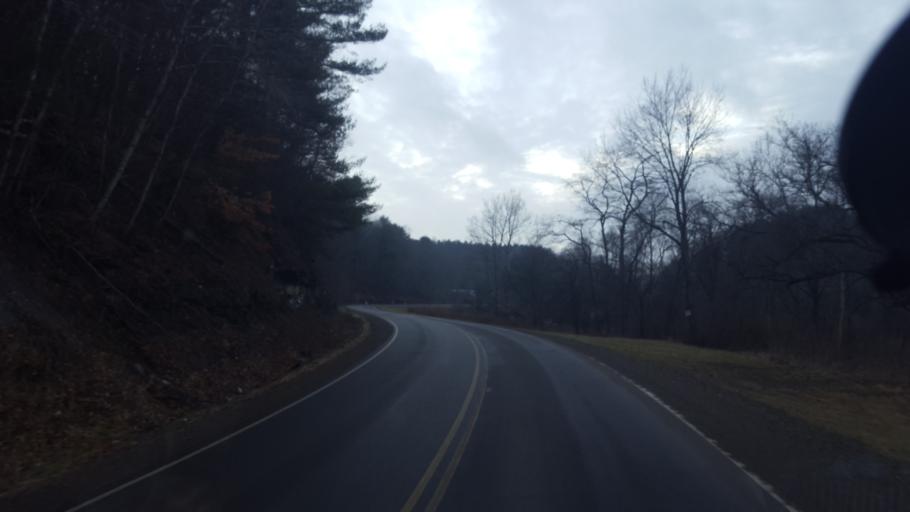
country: US
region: New York
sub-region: Allegany County
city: Andover
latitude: 42.0363
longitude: -77.7579
